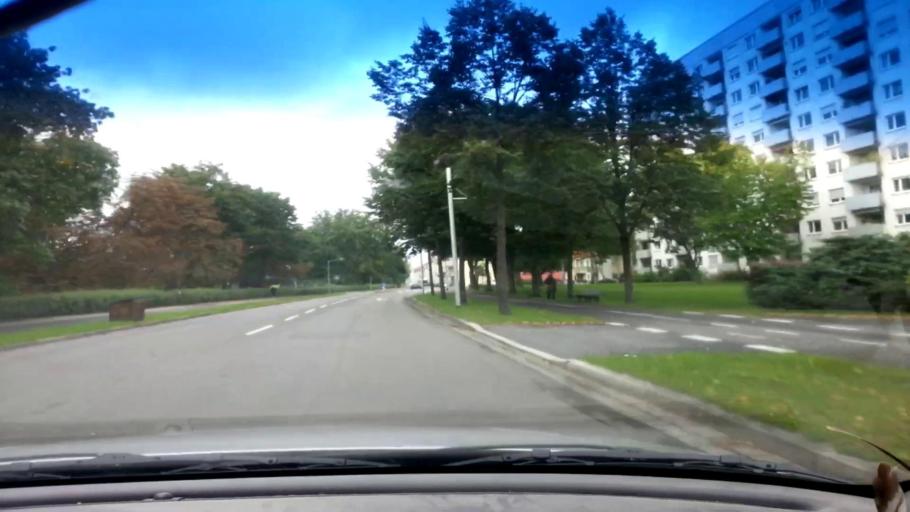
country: DE
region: Bavaria
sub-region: Upper Franconia
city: Bamberg
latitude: 49.8874
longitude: 10.9057
